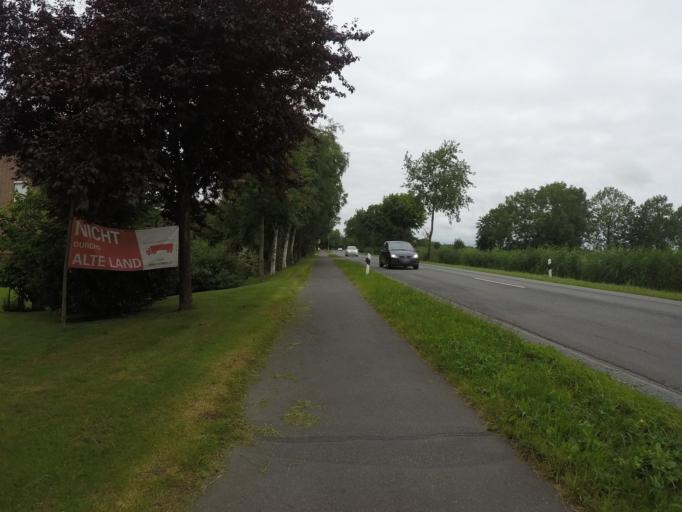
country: DE
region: Lower Saxony
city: Jork
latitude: 53.5375
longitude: 9.7059
